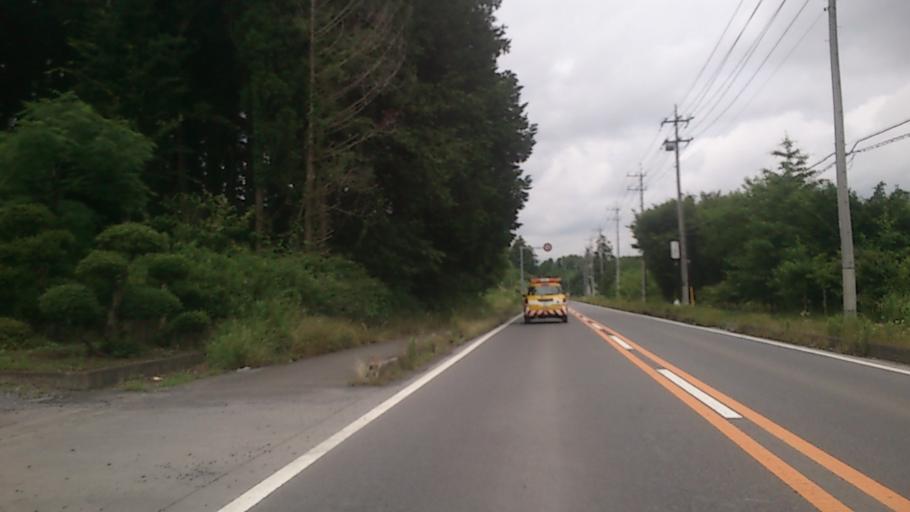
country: JP
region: Ibaraki
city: Okunoya
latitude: 36.2730
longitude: 140.3620
